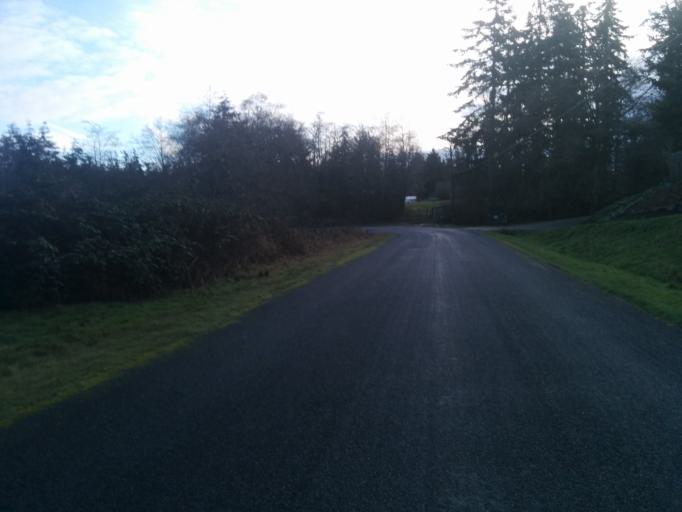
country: US
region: Washington
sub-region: Island County
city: Freeland
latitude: 48.0429
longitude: -122.5004
